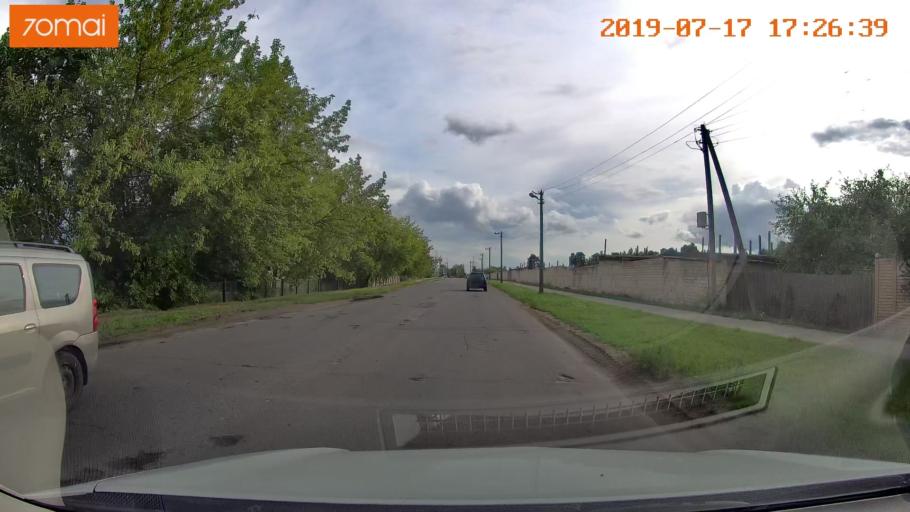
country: BY
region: Mogilev
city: Babruysk
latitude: 53.1399
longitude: 29.1712
